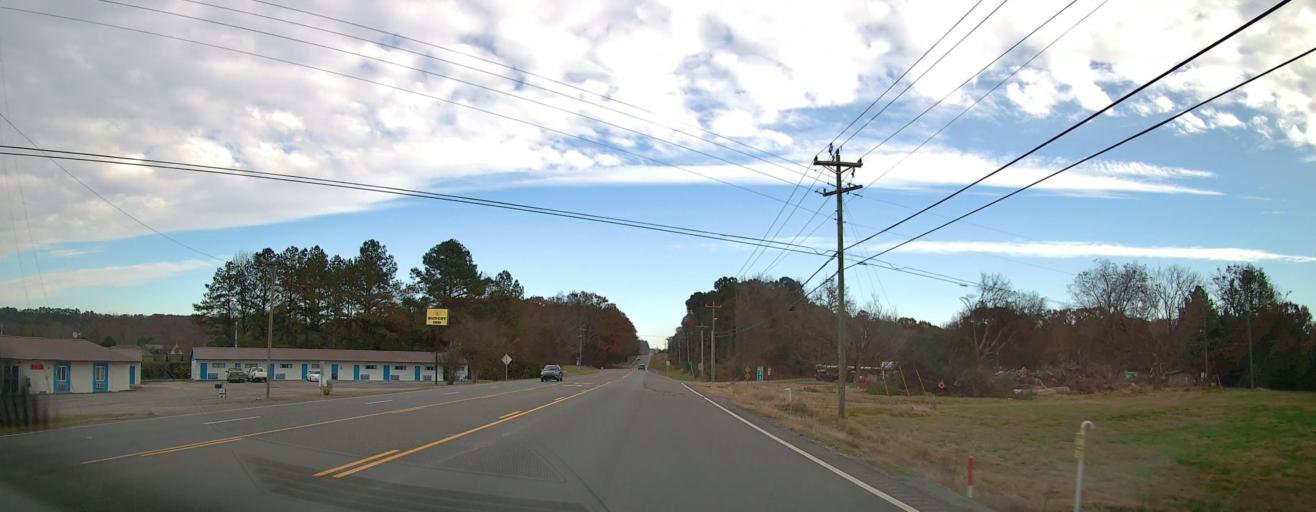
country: US
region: Alabama
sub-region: Morgan County
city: Priceville
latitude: 34.5187
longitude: -86.8864
